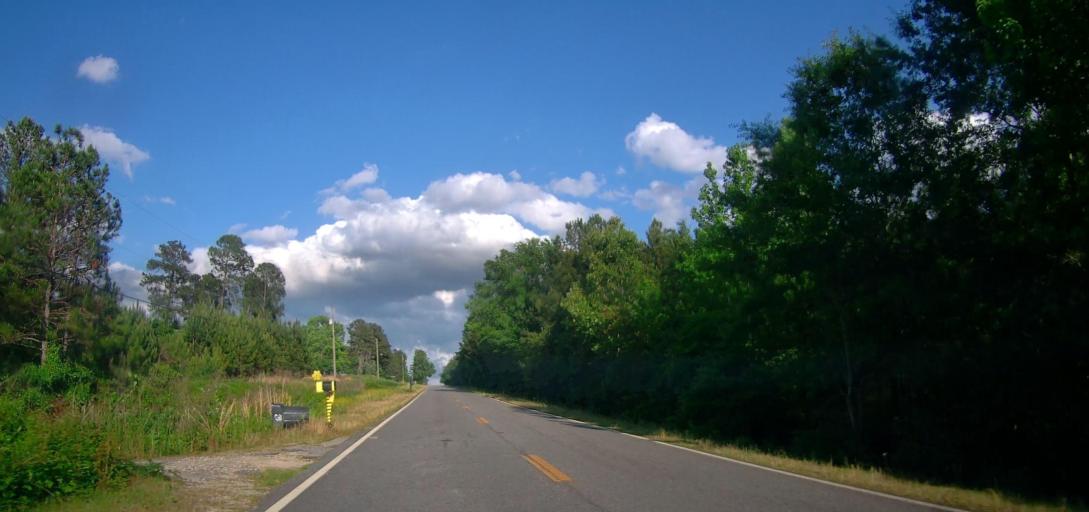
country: US
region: Georgia
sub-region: Peach County
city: Byron
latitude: 32.6771
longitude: -83.7718
